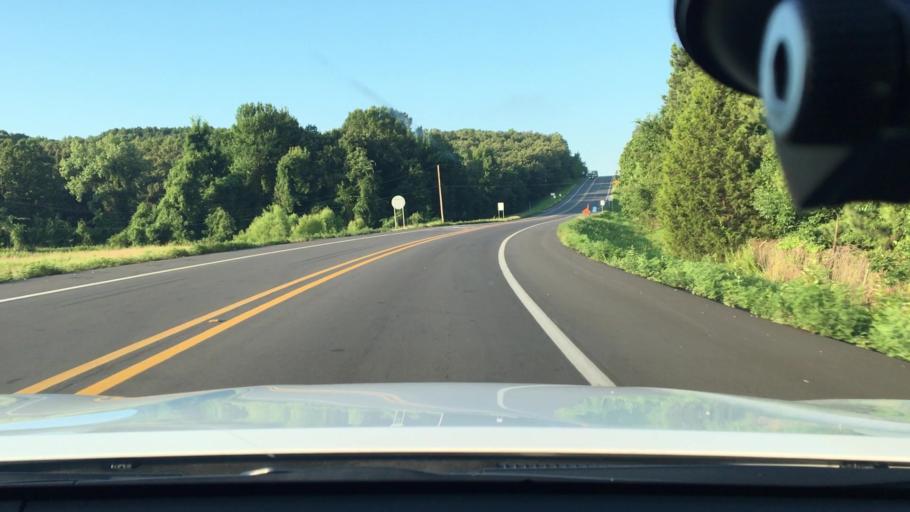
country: US
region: Arkansas
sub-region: Johnson County
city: Clarksville
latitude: 35.4239
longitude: -93.5296
